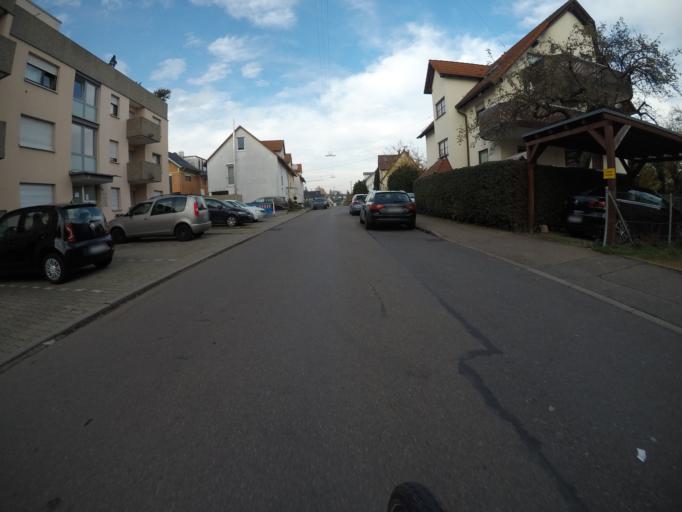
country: DE
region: Baden-Wuerttemberg
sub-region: Regierungsbezirk Stuttgart
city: Leinfelden-Echterdingen
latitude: 48.6847
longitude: 9.1632
